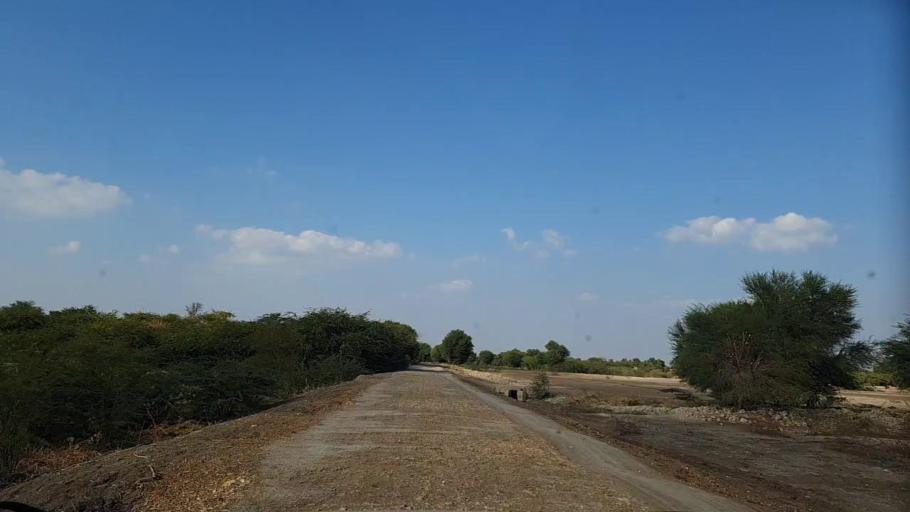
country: PK
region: Sindh
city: Pithoro
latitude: 25.6370
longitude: 69.3511
